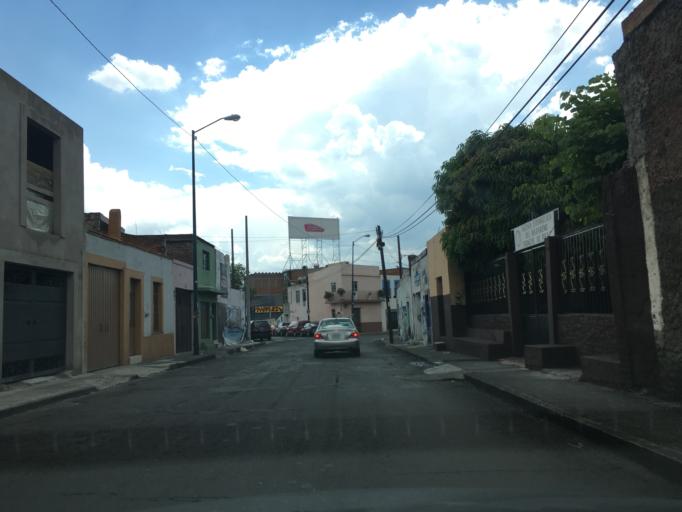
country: MX
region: Michoacan
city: Morelia
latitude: 19.6986
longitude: -101.2009
